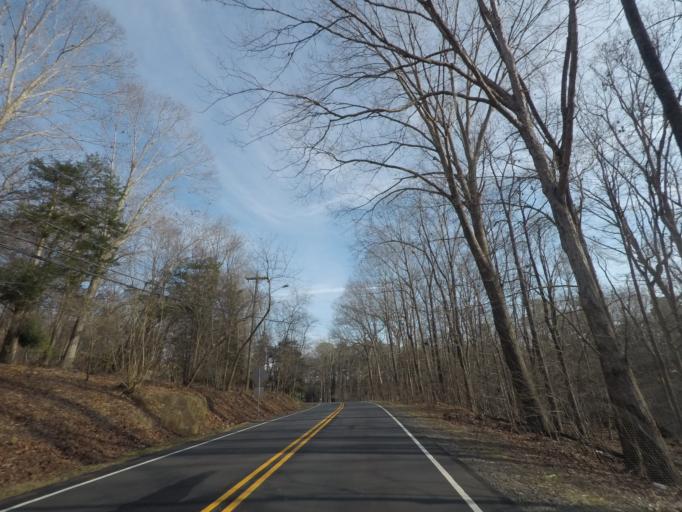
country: US
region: North Carolina
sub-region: Durham County
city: Durham
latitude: 36.0774
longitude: -78.9147
